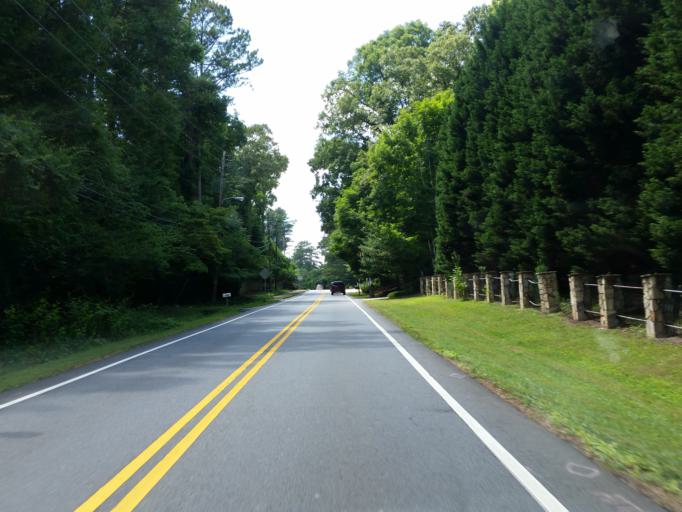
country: US
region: Georgia
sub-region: Fulton County
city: Roswell
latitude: 34.0263
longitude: -84.3741
